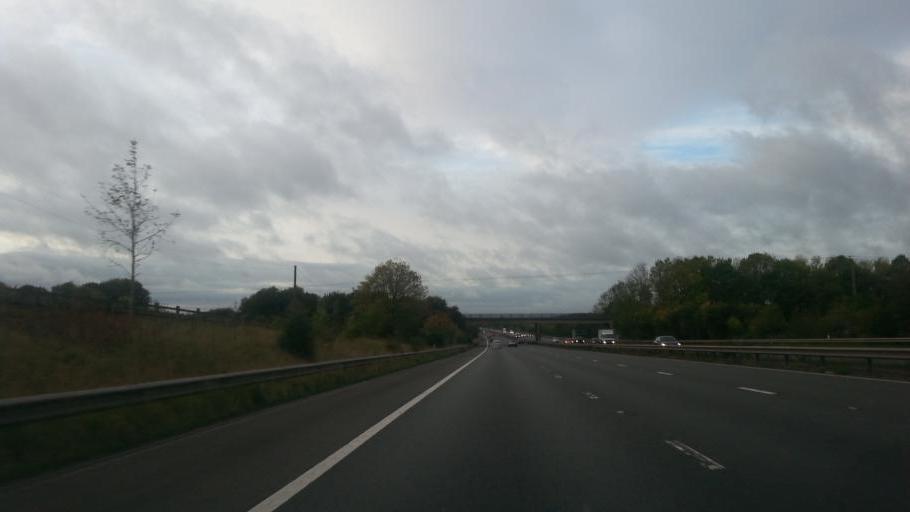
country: GB
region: England
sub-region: Leicestershire
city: Stoney Stanton
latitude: 52.5573
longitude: -1.3003
